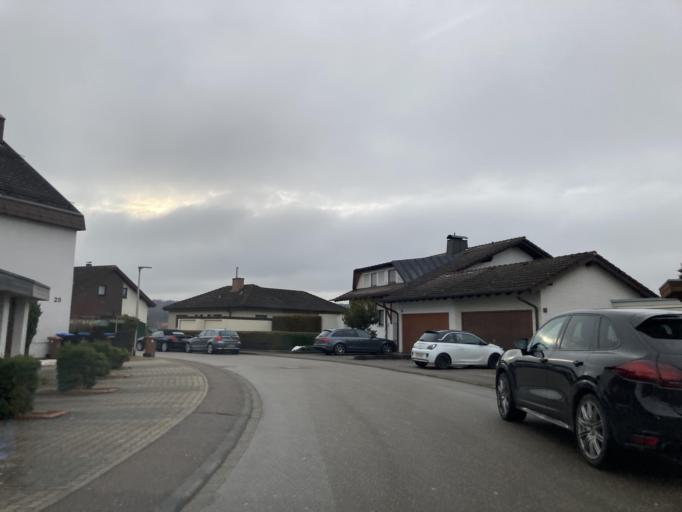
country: DE
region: Baden-Wuerttemberg
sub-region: Regierungsbezirk Stuttgart
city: Bolheim
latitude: 48.6244
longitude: 10.1618
